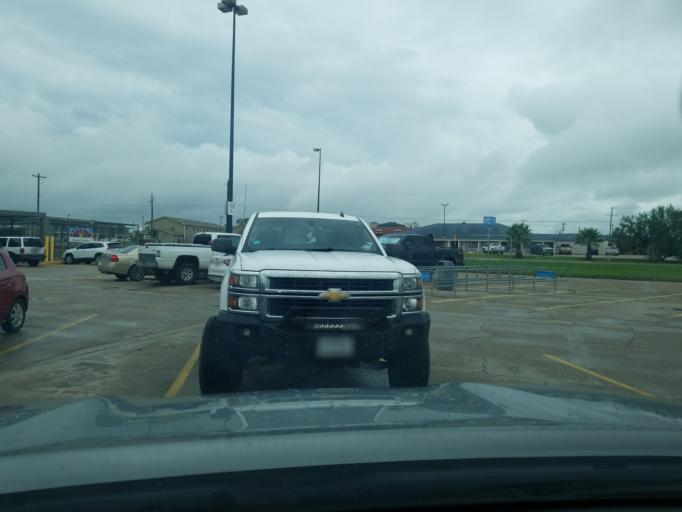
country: US
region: Texas
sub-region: Dimmit County
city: Carrizo Springs
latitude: 28.5424
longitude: -99.8482
